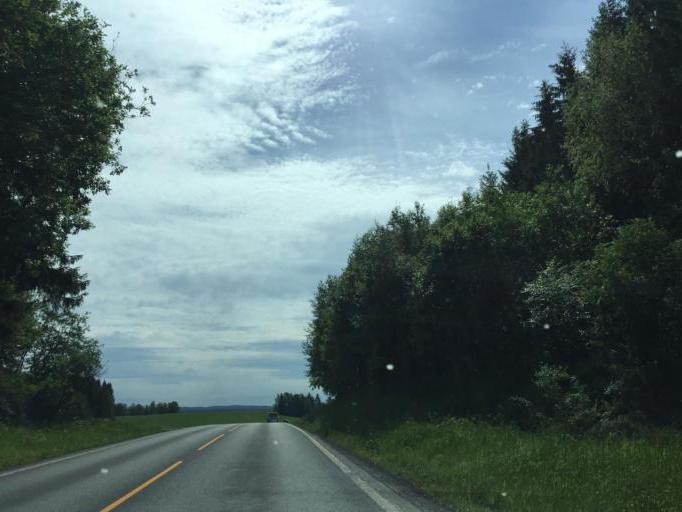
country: NO
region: Akershus
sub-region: Nes
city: Arnes
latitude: 60.1359
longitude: 11.4348
